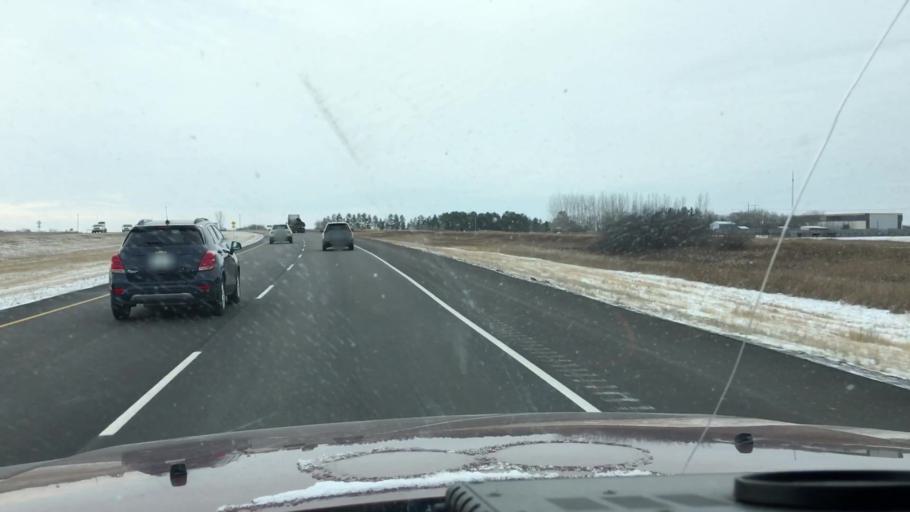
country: CA
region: Saskatchewan
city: Saskatoon
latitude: 51.8580
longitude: -106.5081
